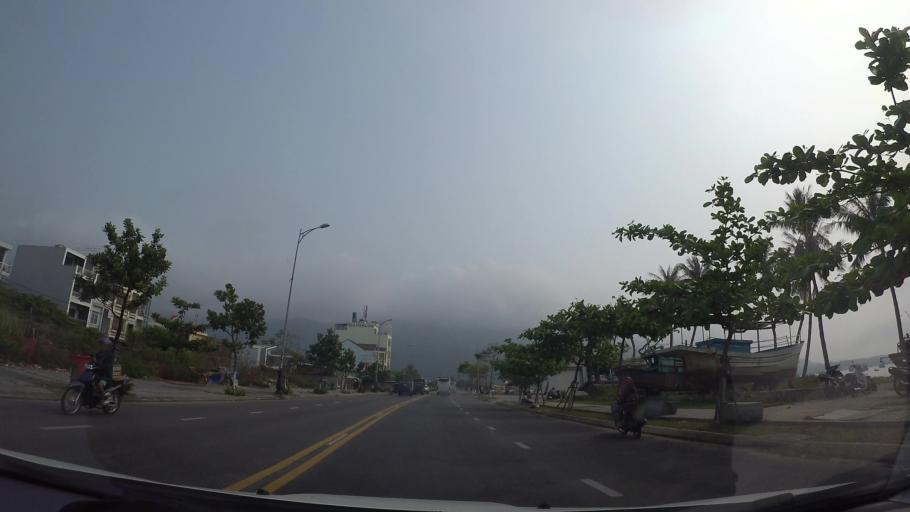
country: VN
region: Da Nang
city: Son Tra
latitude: 16.0986
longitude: 108.2540
